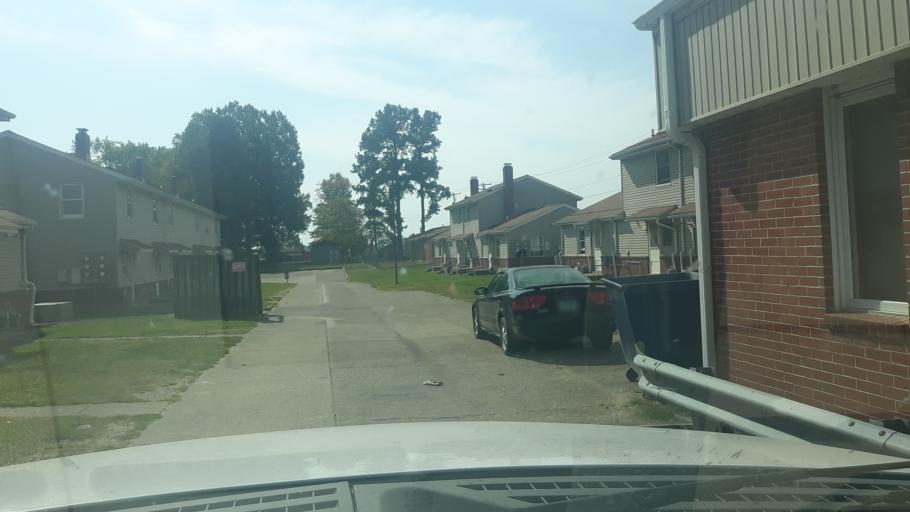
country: US
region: Illinois
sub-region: Saline County
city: Harrisburg
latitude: 37.7201
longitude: -88.5526
